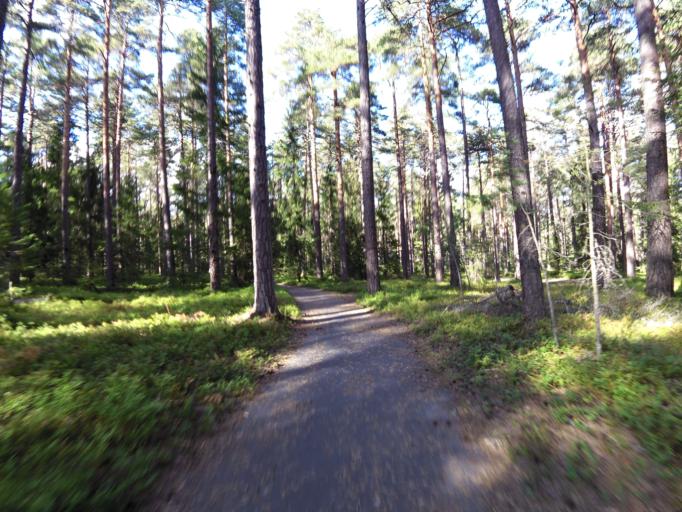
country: SE
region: Gaevleborg
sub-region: Gavle Kommun
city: Gavle
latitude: 60.7105
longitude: 17.1680
